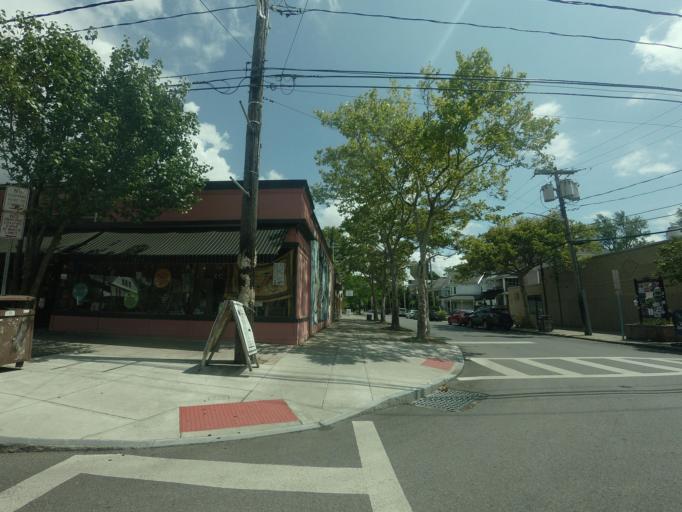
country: US
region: New York
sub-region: Onondaga County
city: Syracuse
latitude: 43.0416
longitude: -76.1193
